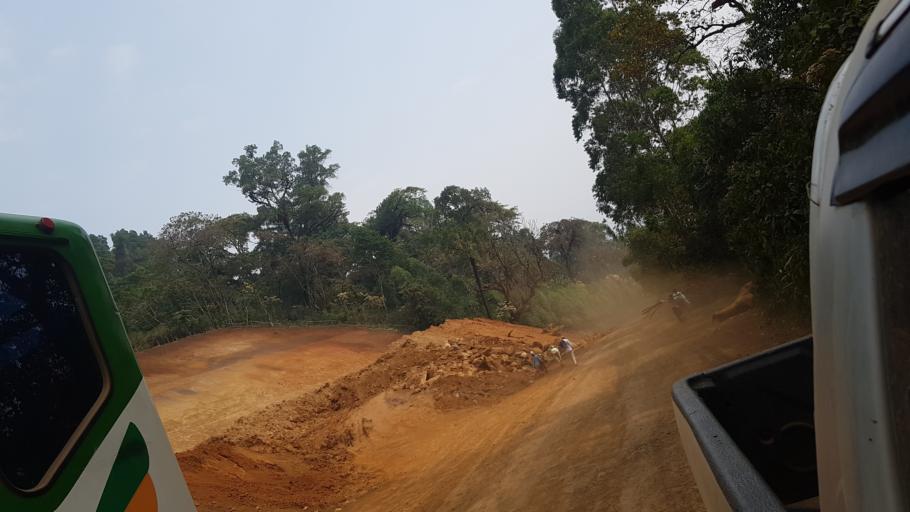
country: ET
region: Oromiya
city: Gore
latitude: 7.8267
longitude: 35.4627
